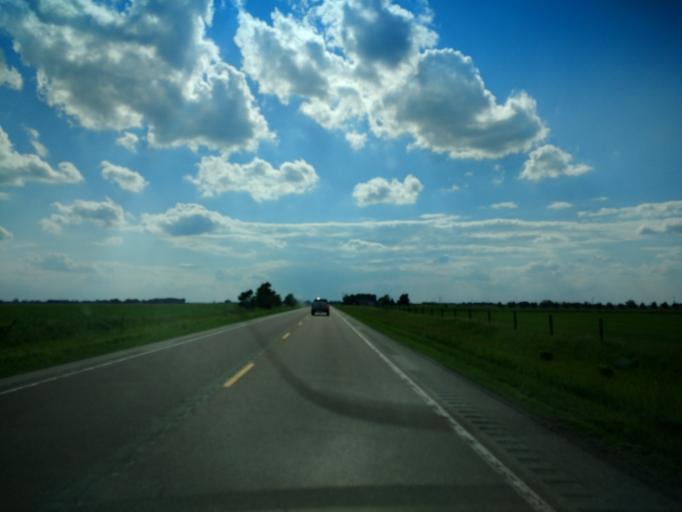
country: US
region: Iowa
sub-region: Clay County
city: Spencer
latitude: 43.1840
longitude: -95.2049
